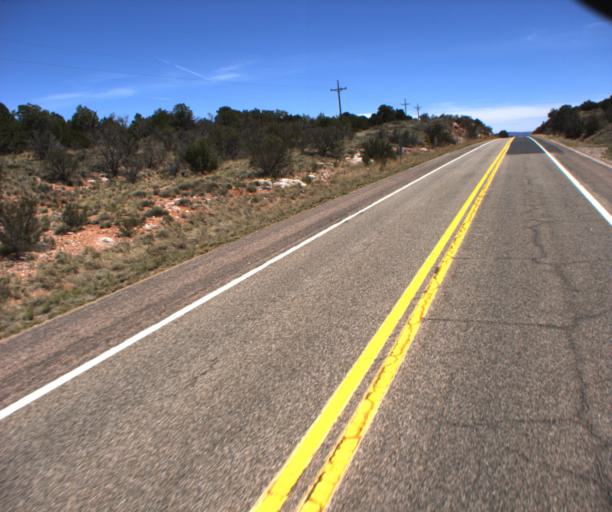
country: US
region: Arizona
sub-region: Mohave County
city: Peach Springs
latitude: 35.5273
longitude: -113.2211
